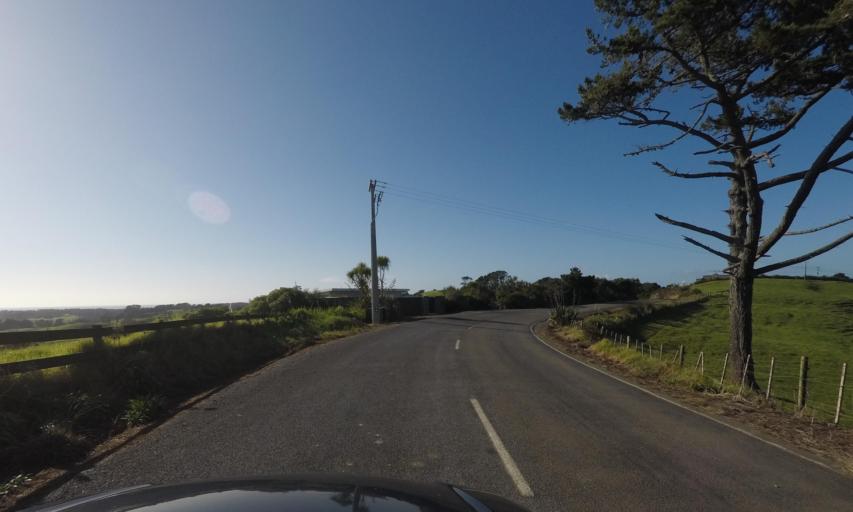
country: NZ
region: Auckland
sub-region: Auckland
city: Wellsford
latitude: -36.1405
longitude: 174.5894
